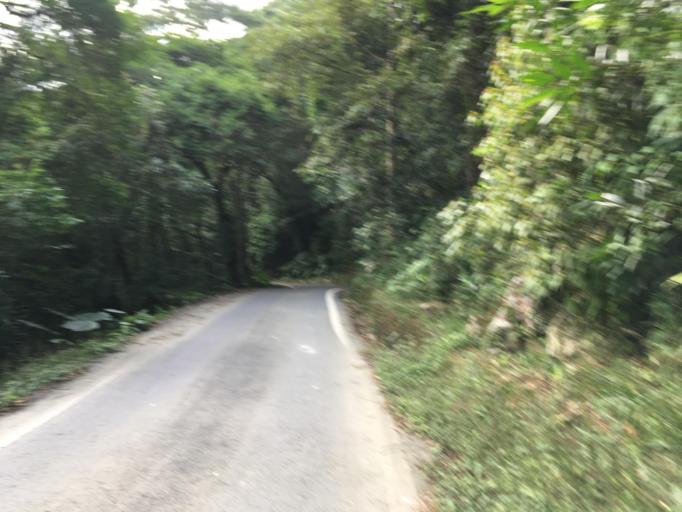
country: TW
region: Taiwan
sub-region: Yilan
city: Yilan
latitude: 24.8425
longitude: 121.7796
